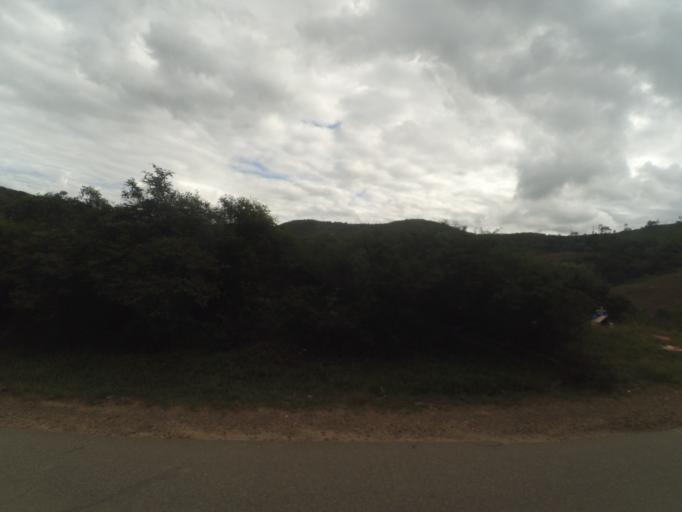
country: BO
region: Santa Cruz
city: Samaipata
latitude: -18.1742
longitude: -63.8505
